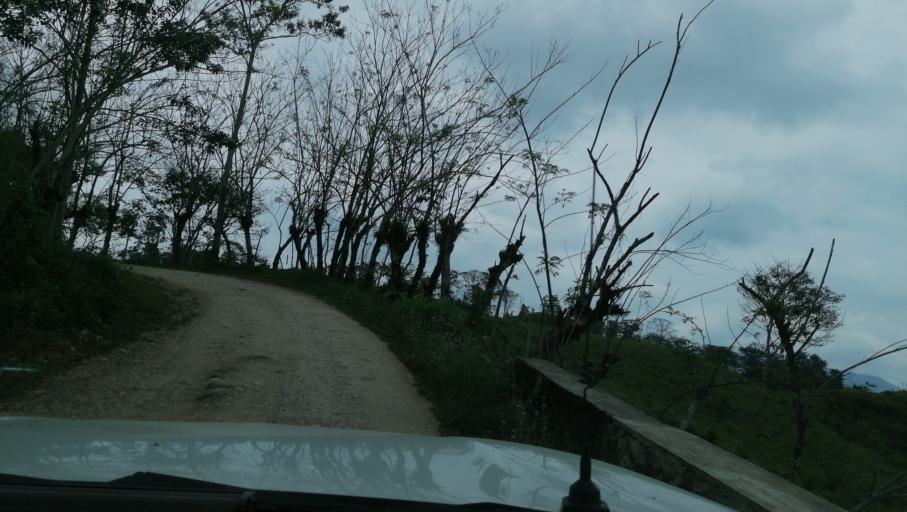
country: MX
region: Chiapas
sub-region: Ocotepec
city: San Pablo Huacano
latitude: 17.2766
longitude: -93.2323
